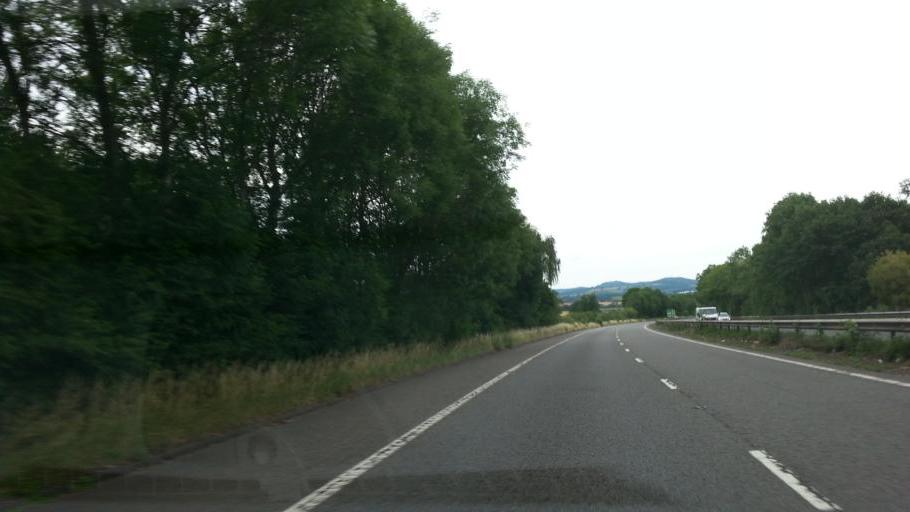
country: GB
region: England
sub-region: Herefordshire
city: Donnington
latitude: 51.9692
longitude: -2.4233
